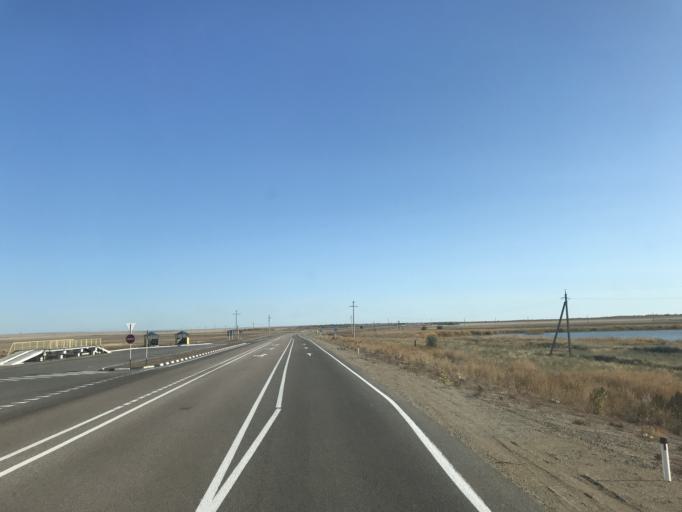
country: KZ
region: Pavlodar
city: Koktobe
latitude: 51.8831
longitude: 77.4175
